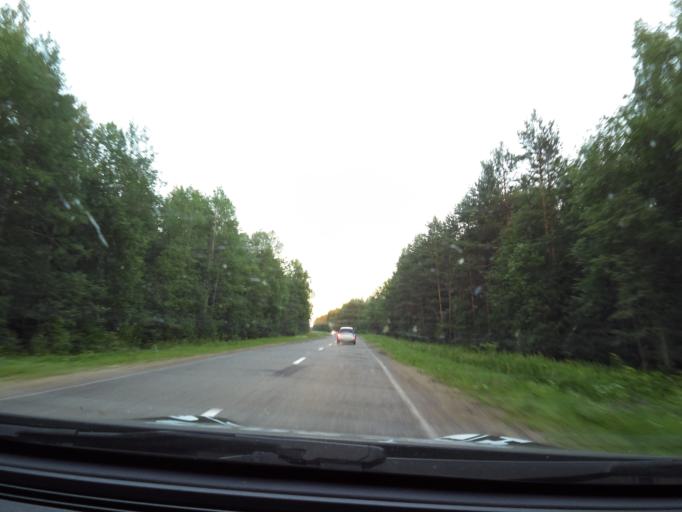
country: RU
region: Jaroslavl
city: Lyubim
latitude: 58.3605
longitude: 40.7674
